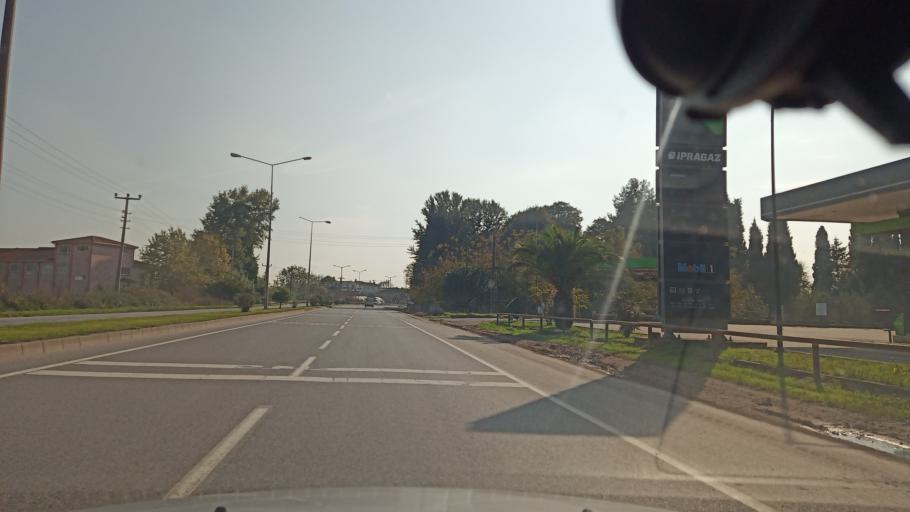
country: TR
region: Sakarya
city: Adapazari
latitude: 40.8138
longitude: 30.4036
